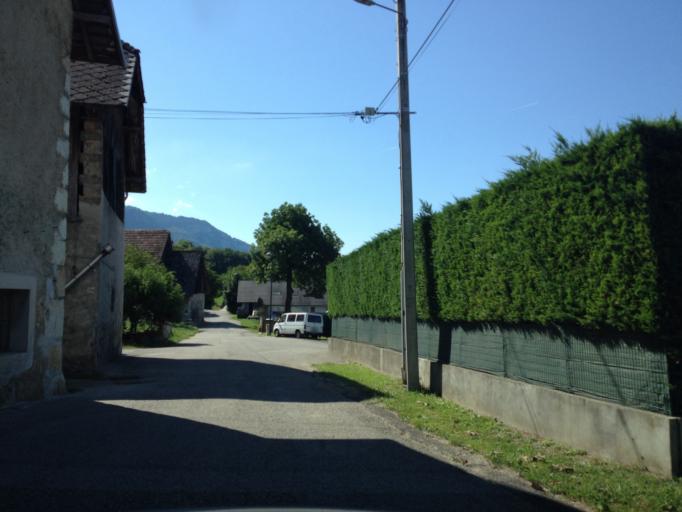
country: FR
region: Rhone-Alpes
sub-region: Departement de la Savoie
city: Mouxy
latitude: 45.6715
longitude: 5.9415
